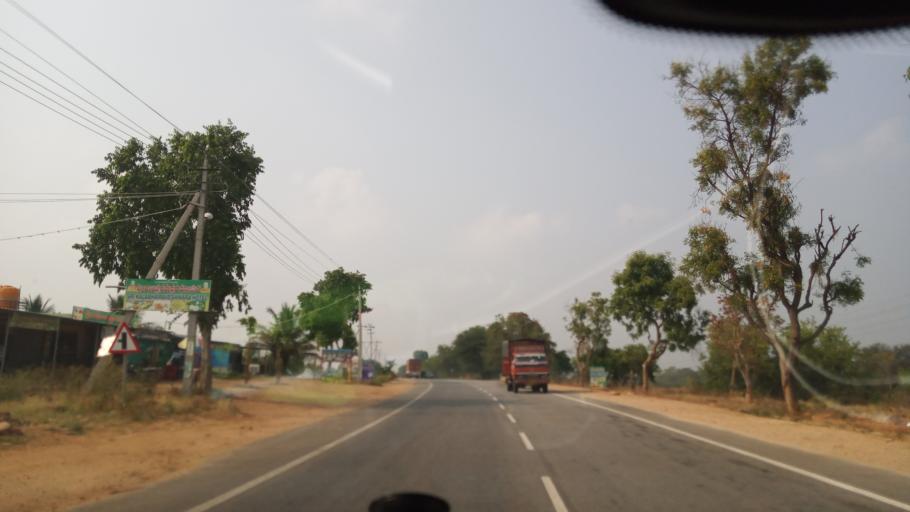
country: IN
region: Karnataka
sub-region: Mandya
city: Nagamangala
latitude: 12.7972
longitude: 76.7512
